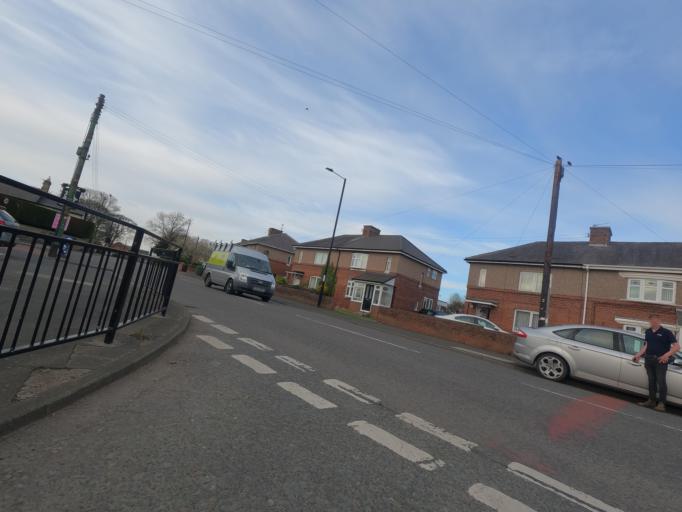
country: GB
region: England
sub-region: Newcastle upon Tyne
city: Dinnington
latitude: 55.0540
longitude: -1.6754
